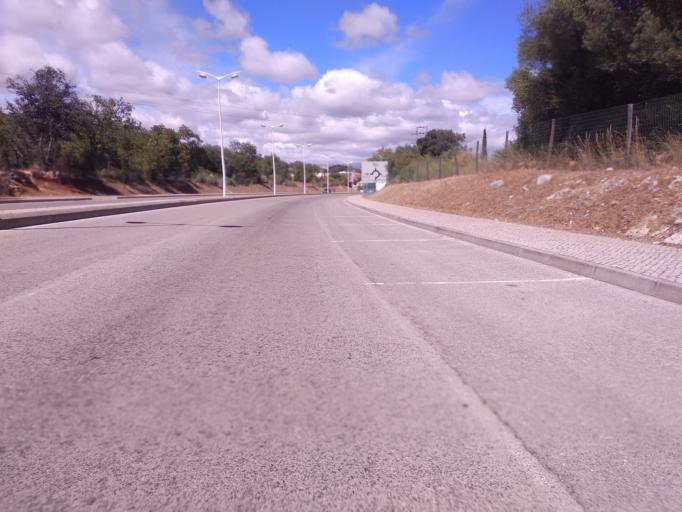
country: PT
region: Faro
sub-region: Sao Bras de Alportel
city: Sao Bras de Alportel
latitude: 37.1565
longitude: -7.8965
